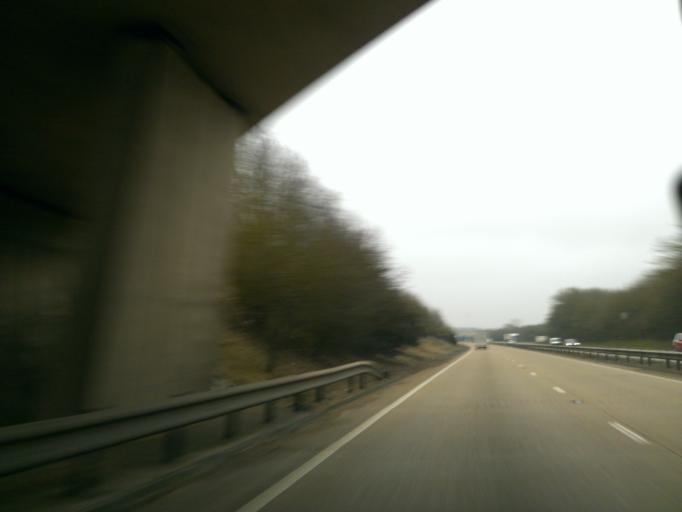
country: GB
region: England
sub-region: Essex
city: Alresford
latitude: 51.8919
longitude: 1.0116
